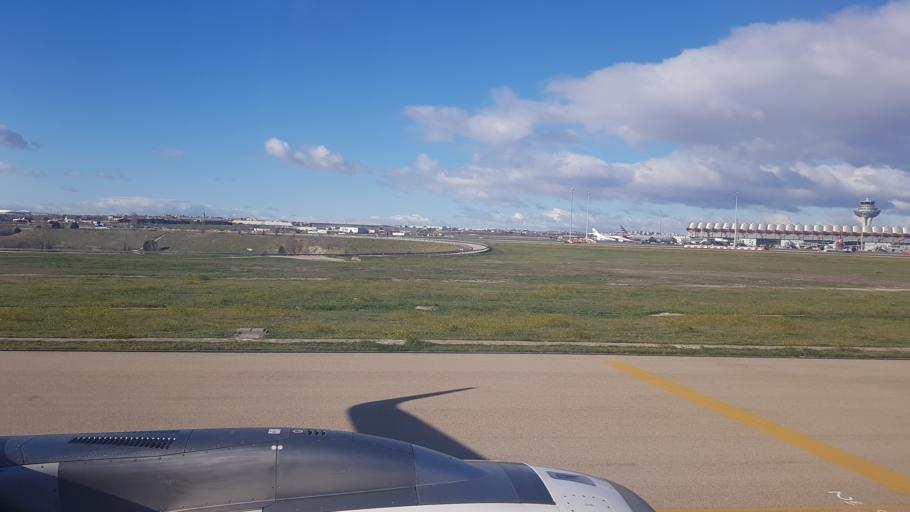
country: ES
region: Madrid
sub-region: Provincia de Madrid
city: Barajas de Madrid
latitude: 40.4913
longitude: -3.5573
